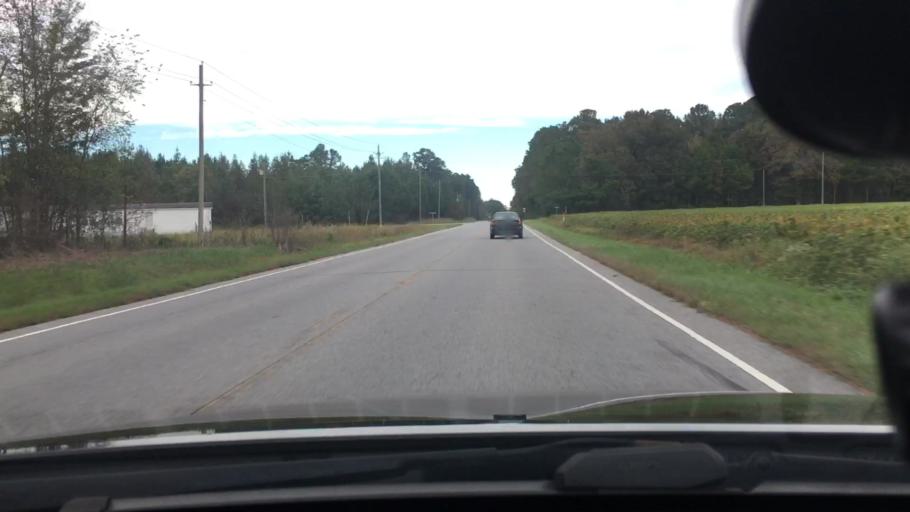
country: US
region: North Carolina
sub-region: Pitt County
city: Windsor
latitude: 35.4375
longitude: -77.2631
